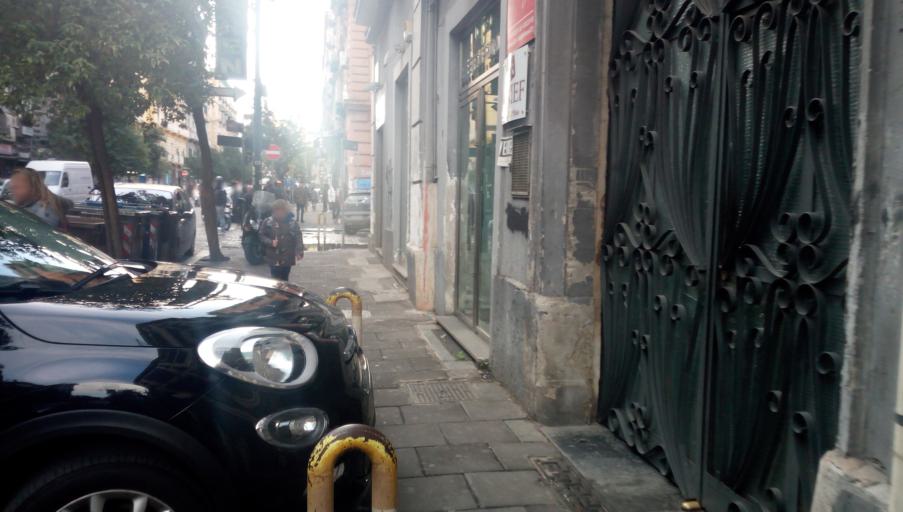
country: IT
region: Campania
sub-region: Provincia di Napoli
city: Napoli
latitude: 40.8543
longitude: 14.2707
